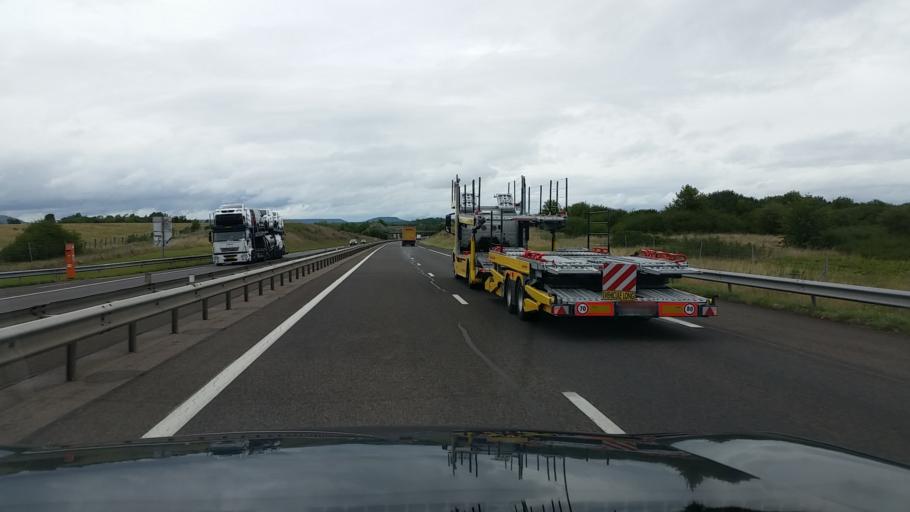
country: FR
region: Lorraine
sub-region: Departement de Meurthe-et-Moselle
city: Blenod-les-Toul
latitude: 48.5968
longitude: 5.8868
